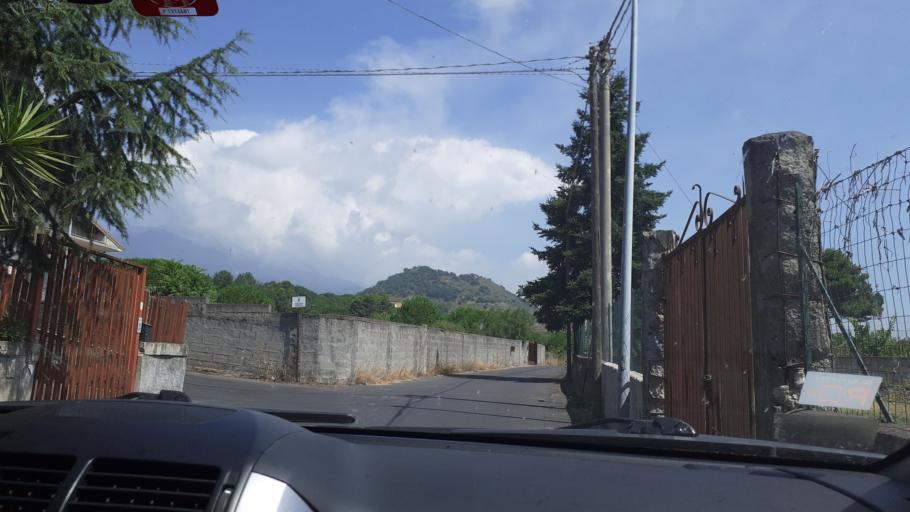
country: IT
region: Sicily
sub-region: Catania
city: Nicolosi
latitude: 37.6191
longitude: 15.0314
